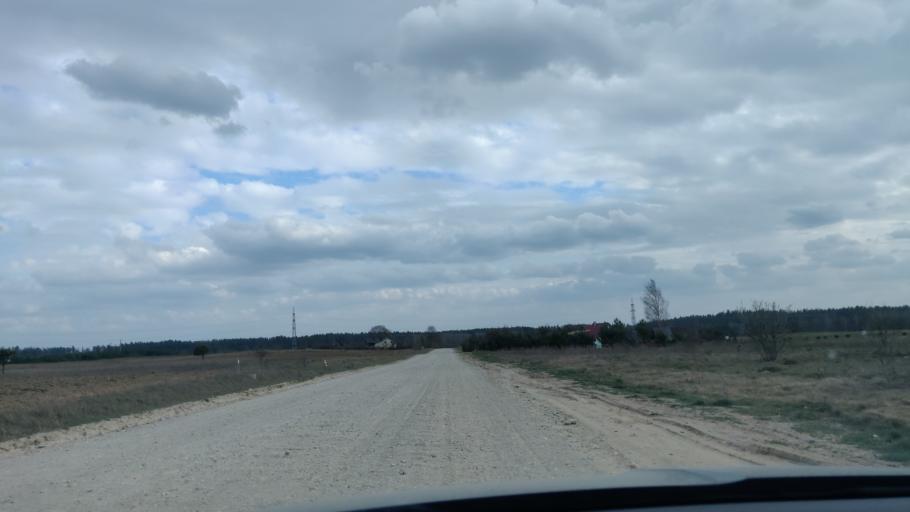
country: LT
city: Lentvaris
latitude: 54.6135
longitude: 25.0694
